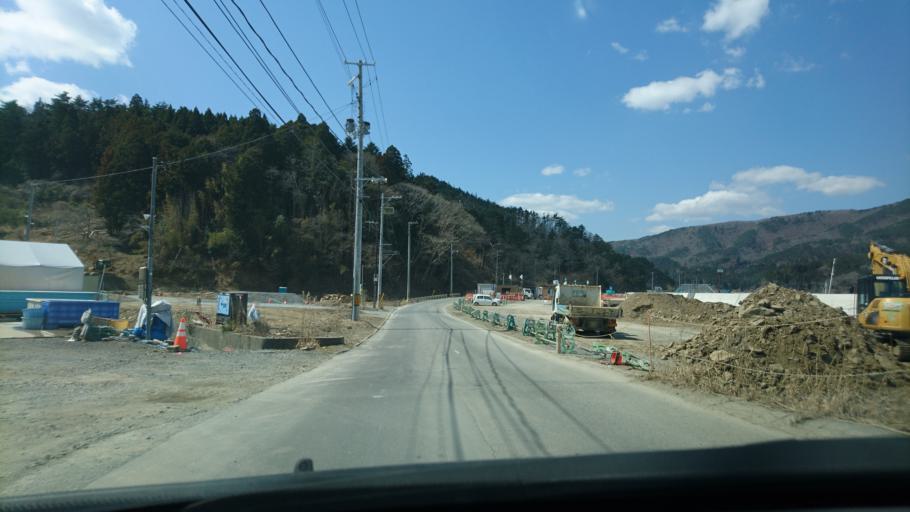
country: JP
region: Miyagi
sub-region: Oshika Gun
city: Onagawa Cho
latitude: 38.5128
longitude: 141.4796
